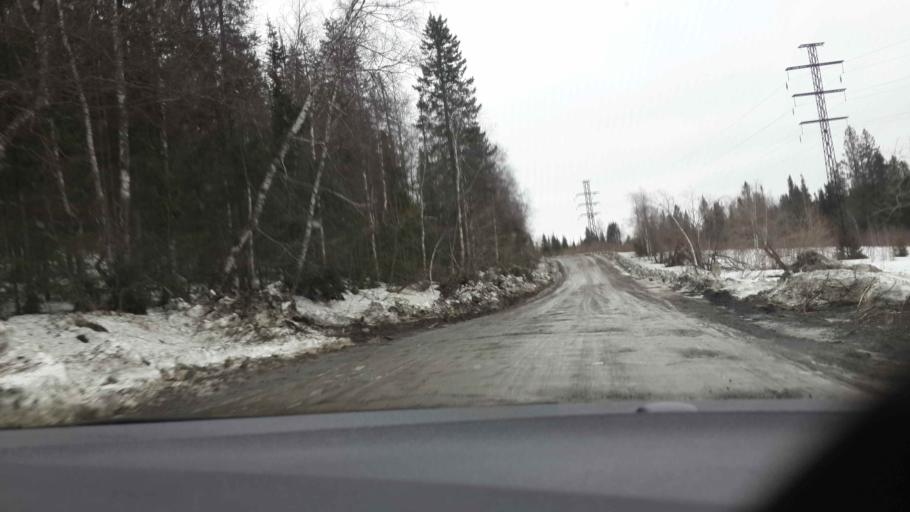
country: RU
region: Chelyabinsk
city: Magnitka
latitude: 55.2665
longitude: 59.6996
